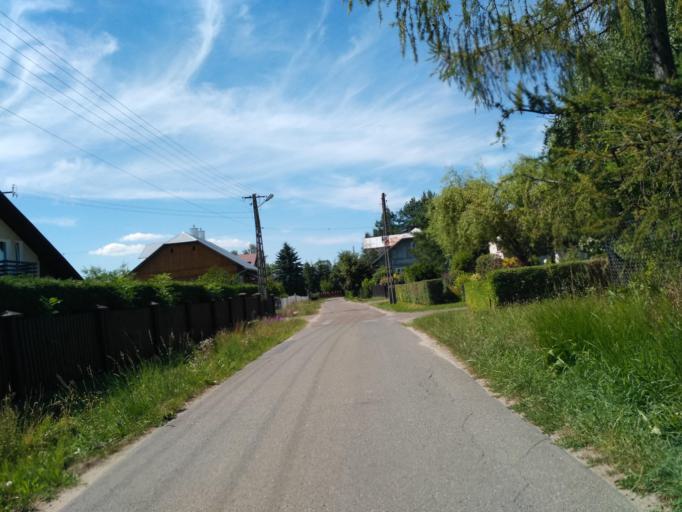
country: PL
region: Subcarpathian Voivodeship
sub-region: Powiat brzozowski
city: Brzozow
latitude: 49.6976
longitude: 22.0276
